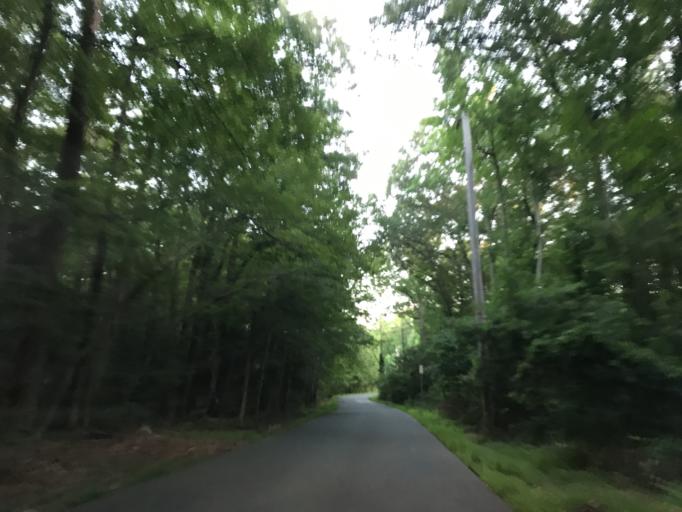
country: US
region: Maryland
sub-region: Baltimore County
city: Bowleys Quarters
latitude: 39.3388
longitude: -76.3813
